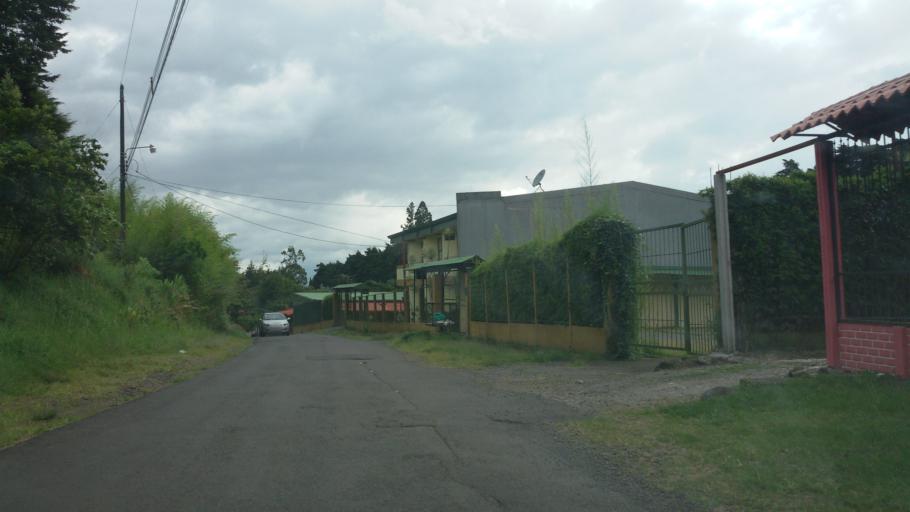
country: CR
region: Heredia
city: Angeles
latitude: 10.0324
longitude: -84.0201
